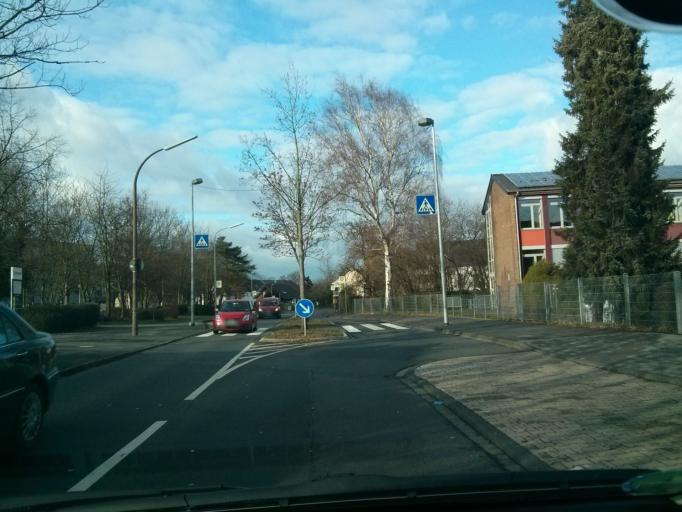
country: DE
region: North Rhine-Westphalia
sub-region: Regierungsbezirk Koln
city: Hennef
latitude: 50.7770
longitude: 7.2750
